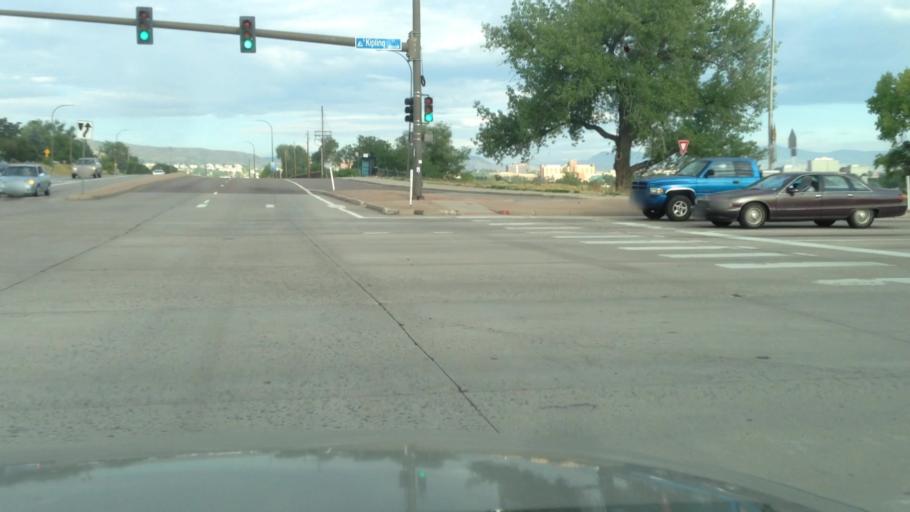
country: US
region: Colorado
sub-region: Jefferson County
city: Lakewood
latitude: 39.7111
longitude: -105.1095
